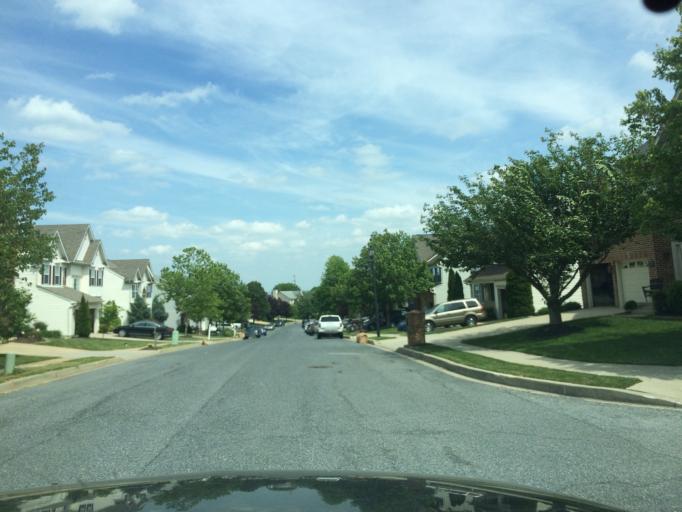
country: US
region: Maryland
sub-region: Carroll County
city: Sykesville
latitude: 39.3797
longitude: -76.9813
